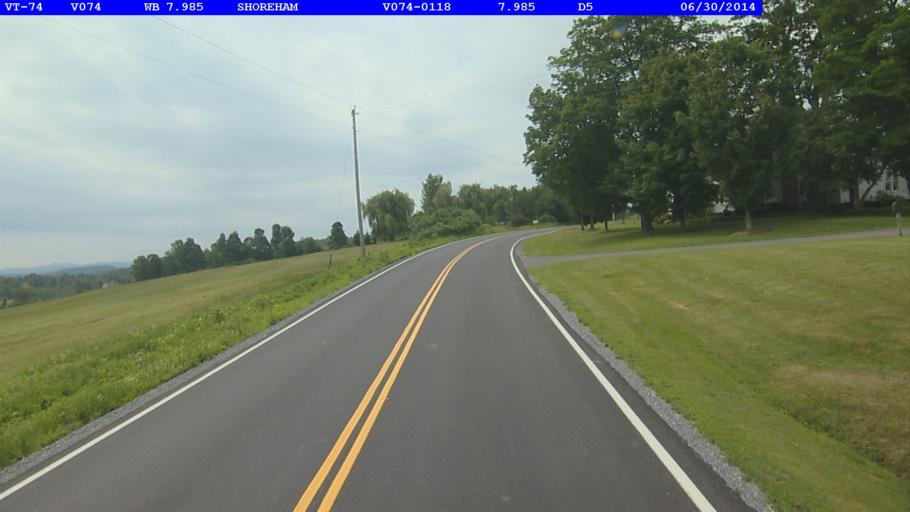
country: US
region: Vermont
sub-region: Addison County
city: Middlebury (village)
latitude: 43.9332
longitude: -73.2874
